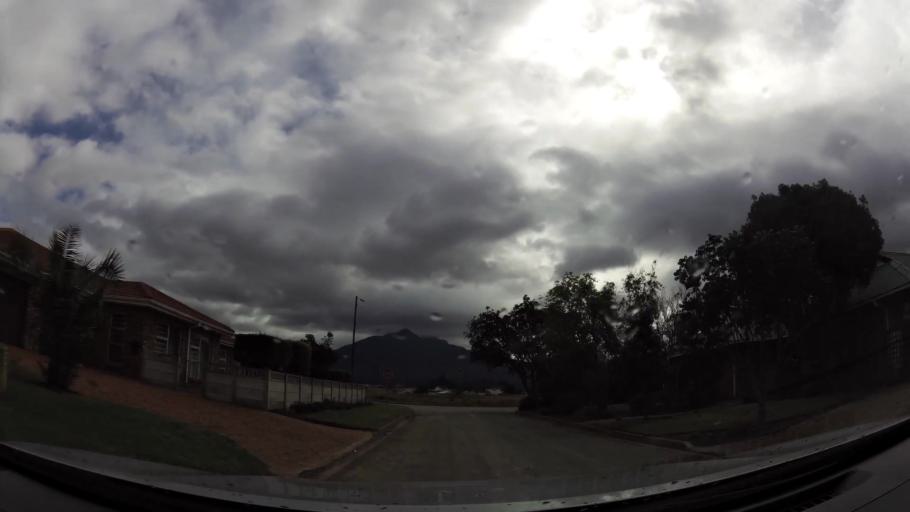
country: ZA
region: Western Cape
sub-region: Eden District Municipality
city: George
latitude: -33.9758
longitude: 22.4905
